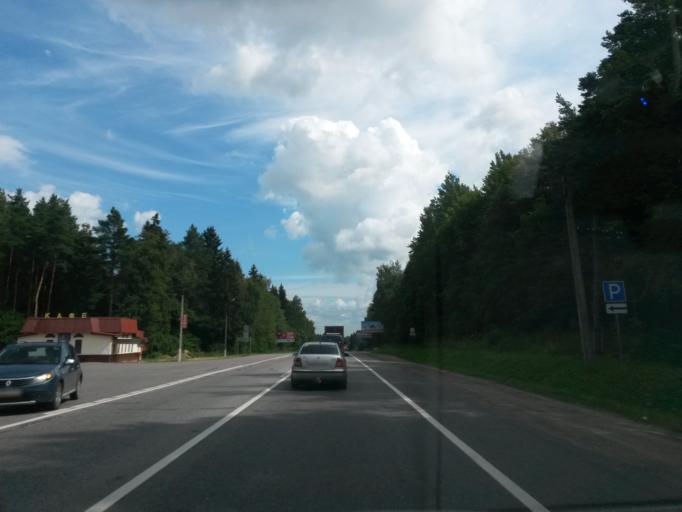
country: RU
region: Jaroslavl
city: Pereslavl'-Zalesskiy
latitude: 56.6981
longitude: 38.7746
